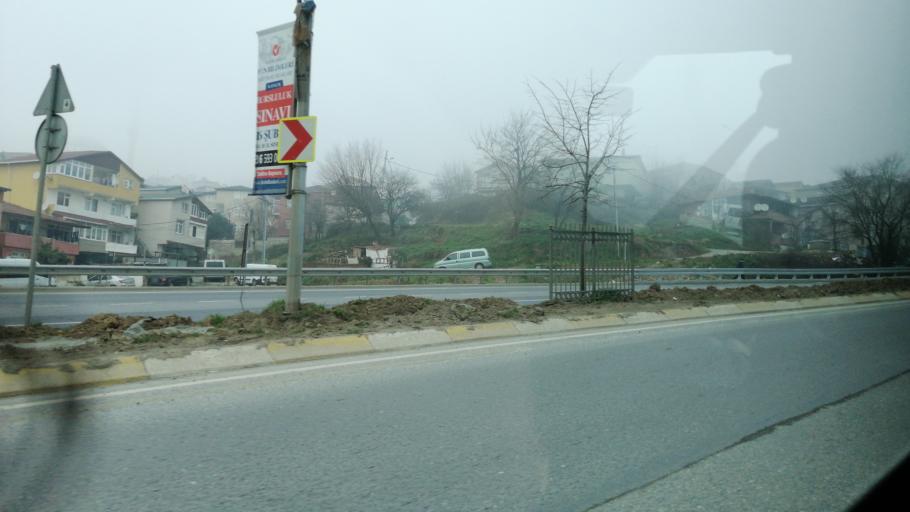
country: TR
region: Istanbul
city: Umraniye
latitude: 41.0871
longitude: 29.0854
